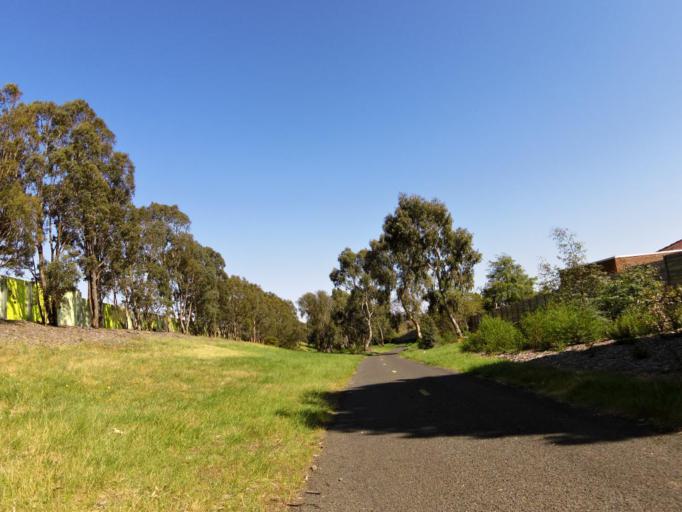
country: AU
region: Victoria
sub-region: Banyule
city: Bundoora
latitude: -37.6858
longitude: 145.0642
